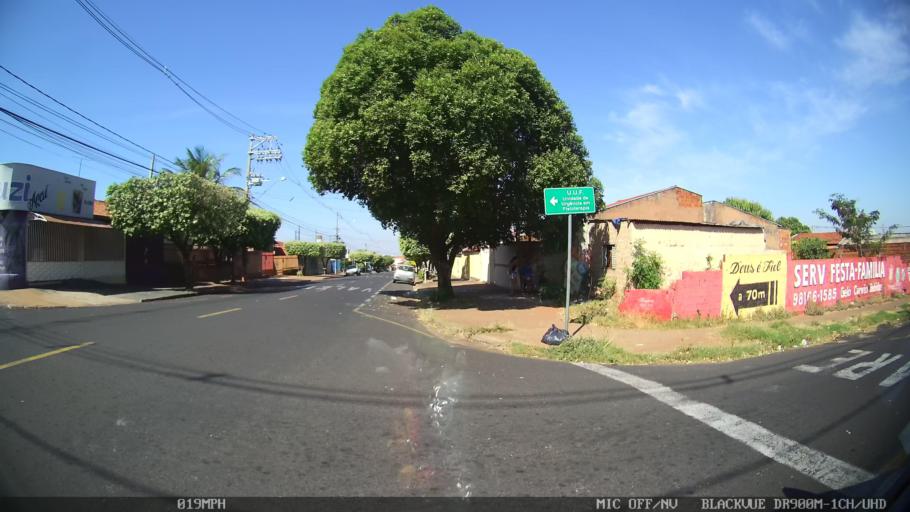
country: BR
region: Sao Paulo
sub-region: Sao Jose Do Rio Preto
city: Sao Jose do Rio Preto
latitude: -20.7833
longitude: -49.4116
